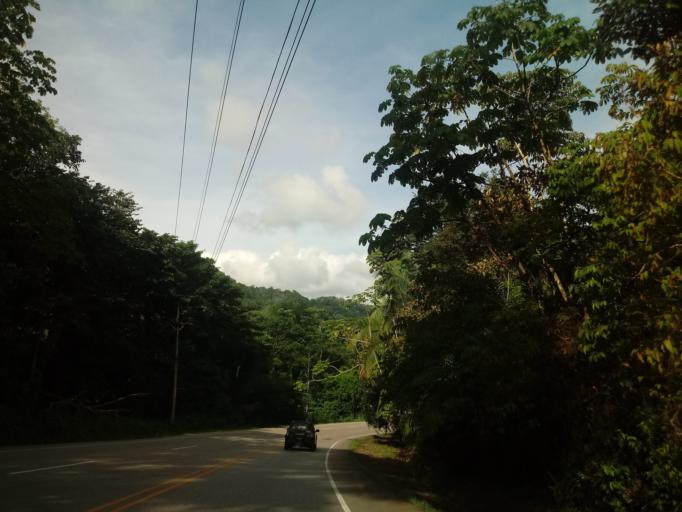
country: CR
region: San Jose
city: Daniel Flores
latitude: 9.2003
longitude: -83.7862
